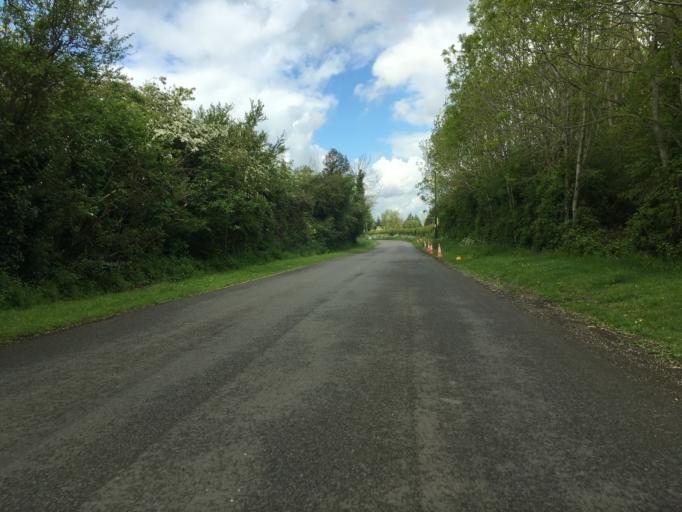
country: GB
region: England
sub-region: Gloucestershire
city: Stonehouse
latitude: 51.7802
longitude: -2.3117
